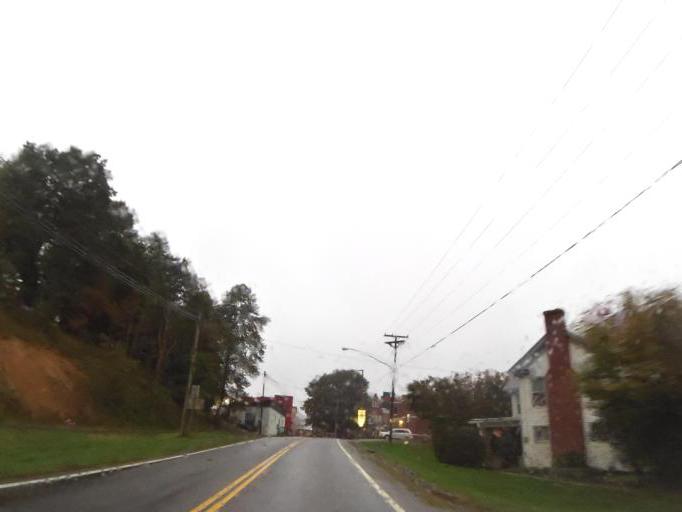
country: US
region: Virginia
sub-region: Grayson County
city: Independence
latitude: 36.6238
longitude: -81.1533
